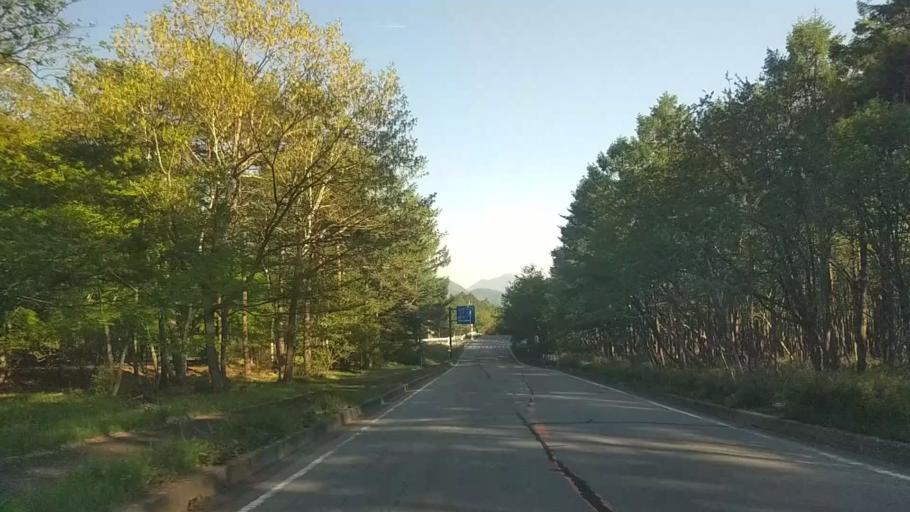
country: JP
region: Yamanashi
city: Nirasaki
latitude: 35.9239
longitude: 138.4329
